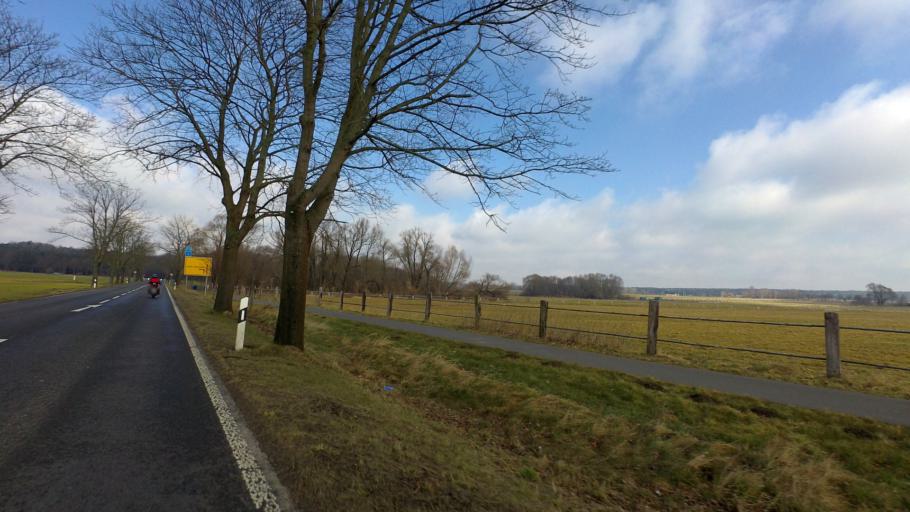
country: DE
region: Brandenburg
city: Glienicke
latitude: 52.6595
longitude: 13.3302
